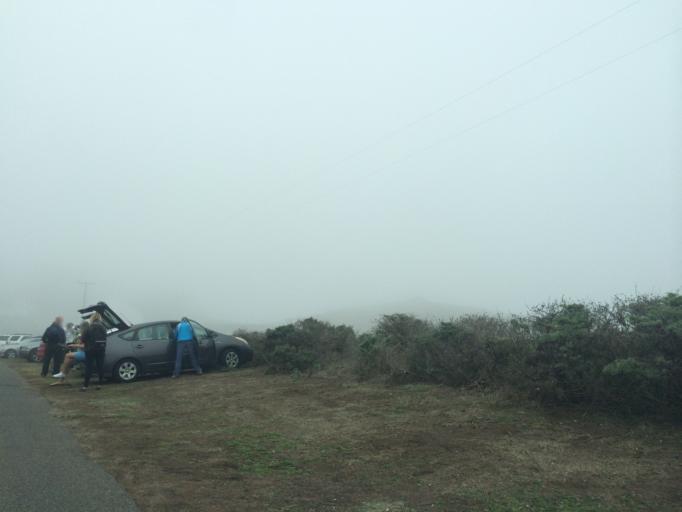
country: US
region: California
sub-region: Marin County
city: Inverness
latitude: 38.1882
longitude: -122.9535
